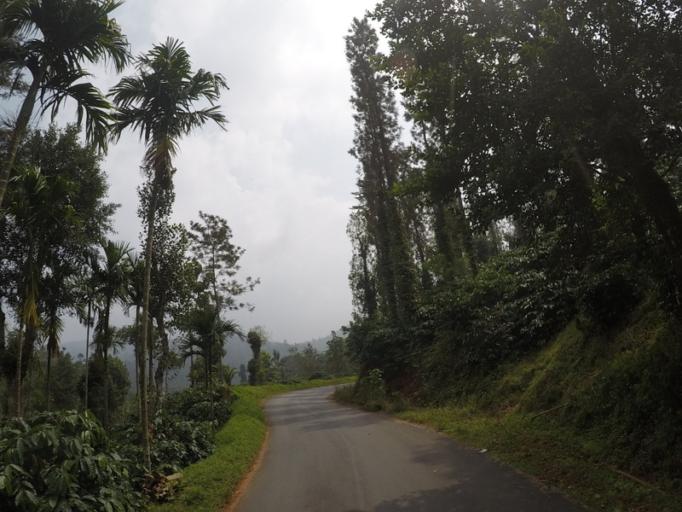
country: IN
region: Karnataka
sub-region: Chikmagalur
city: Mudigere
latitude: 13.1596
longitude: 75.4420
